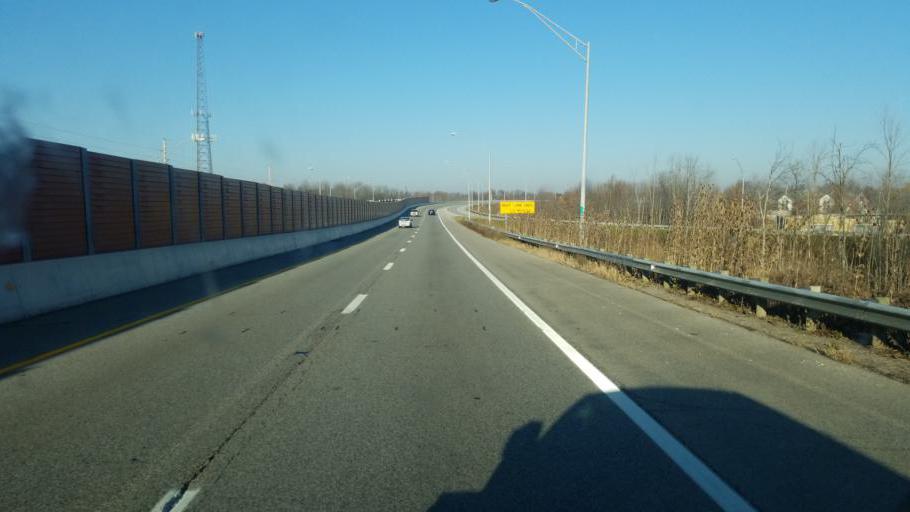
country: US
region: Ohio
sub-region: Summit County
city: Macedonia
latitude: 41.2950
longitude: -81.5142
